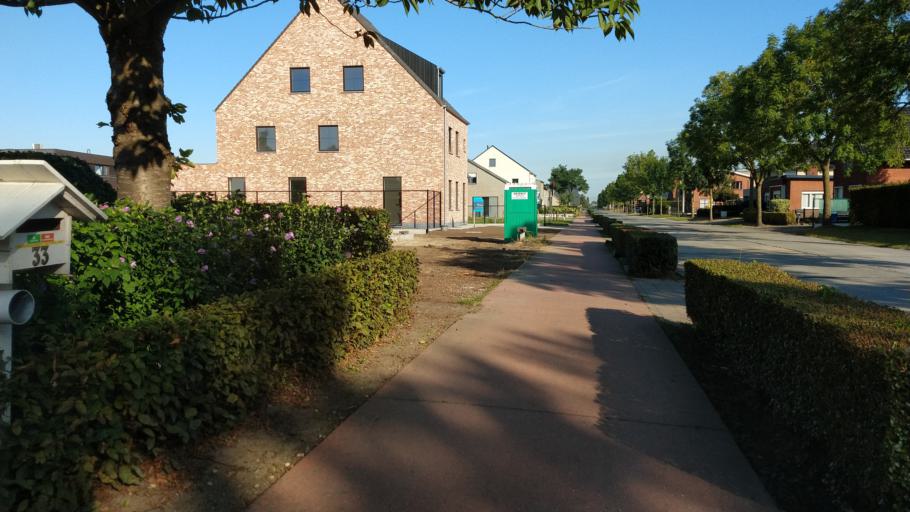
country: BE
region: Flanders
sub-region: Provincie Oost-Vlaanderen
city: Lochristi
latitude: 51.1014
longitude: 3.8427
